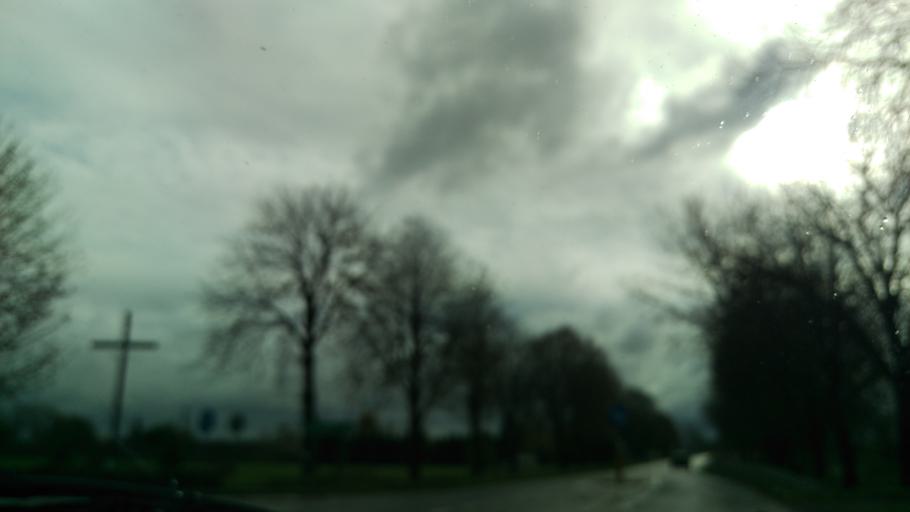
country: PL
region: West Pomeranian Voivodeship
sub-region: Powiat gryficki
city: Ploty
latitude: 53.8215
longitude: 15.2518
